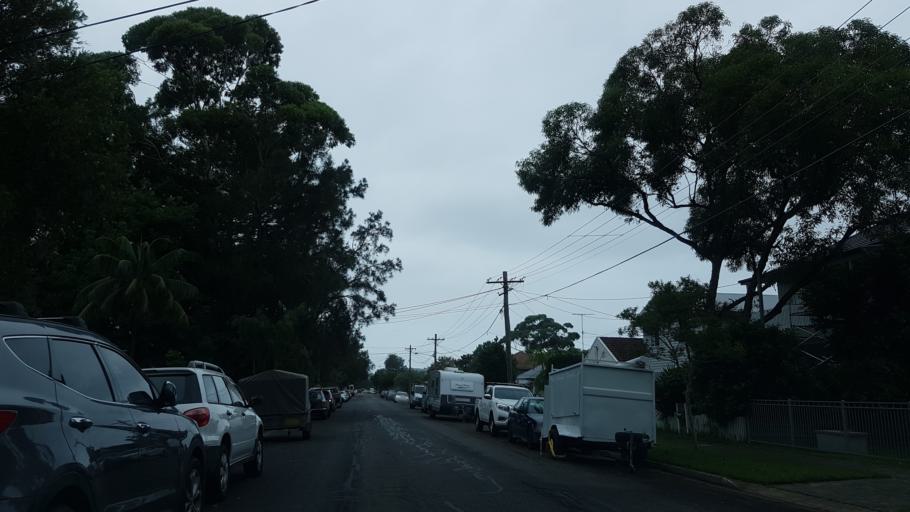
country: AU
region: New South Wales
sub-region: Pittwater
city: North Narrabeen
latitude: -33.7074
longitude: 151.2920
